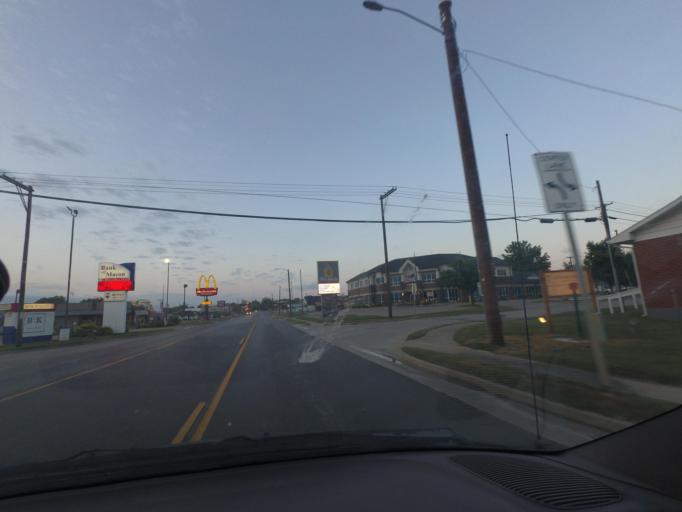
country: US
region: Missouri
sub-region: Macon County
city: Macon
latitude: 39.7510
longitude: -92.4679
